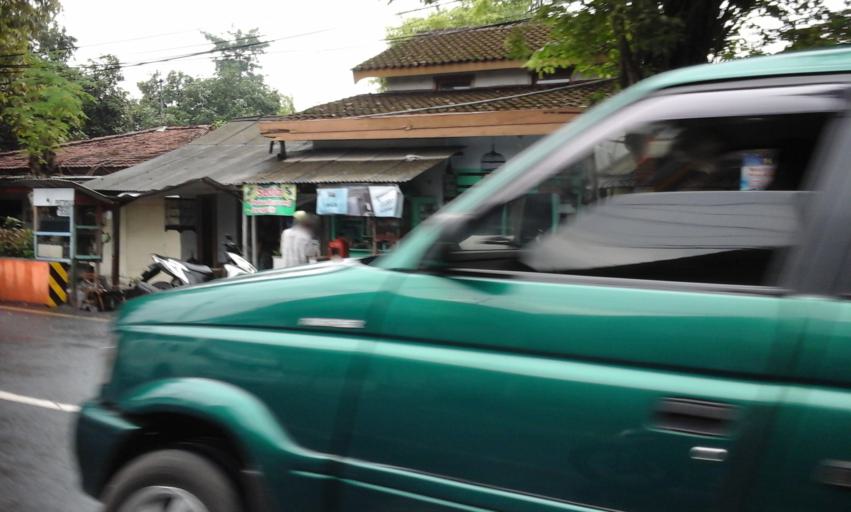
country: ID
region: East Java
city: Lumajang
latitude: -8.1389
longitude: 113.2290
